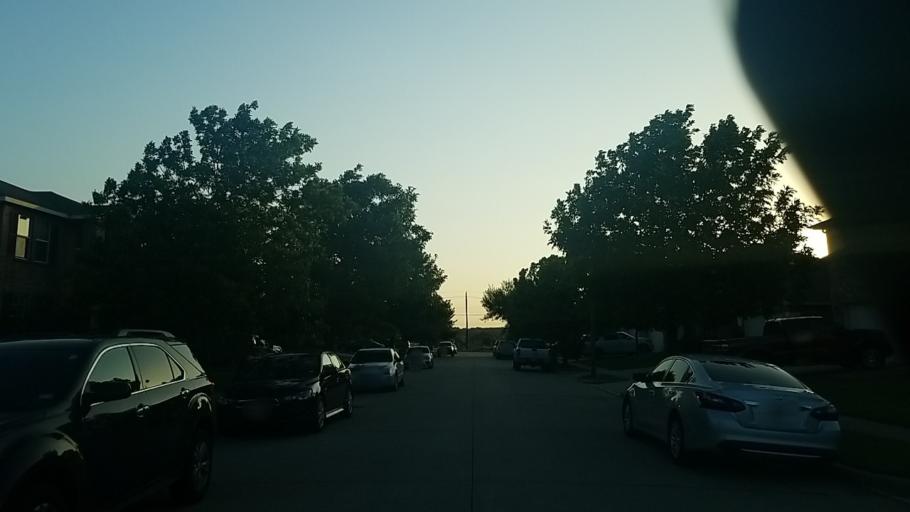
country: US
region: Texas
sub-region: Denton County
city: Corinth
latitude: 33.1516
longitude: -97.1036
